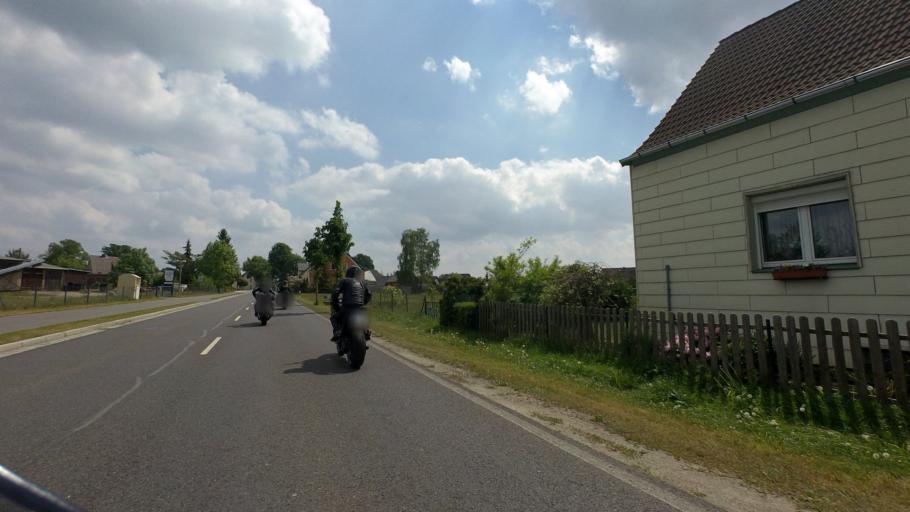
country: DE
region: Saxony
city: Weisskeissel
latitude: 51.4957
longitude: 14.7176
